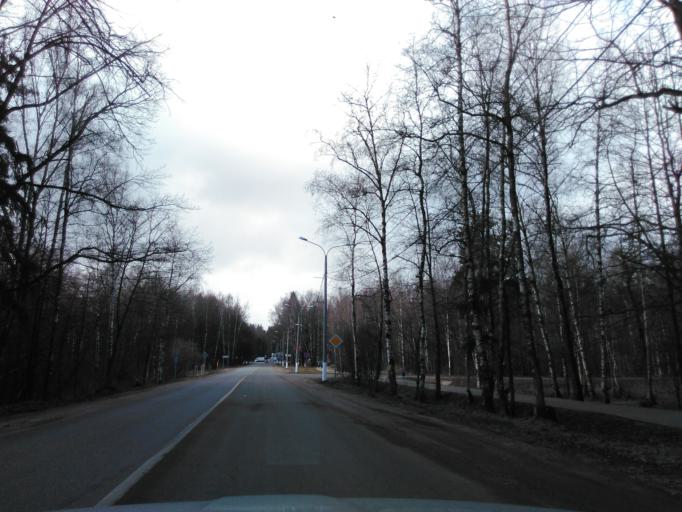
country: RU
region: Moskovskaya
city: Mendeleyevo
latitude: 56.0121
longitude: 37.2220
